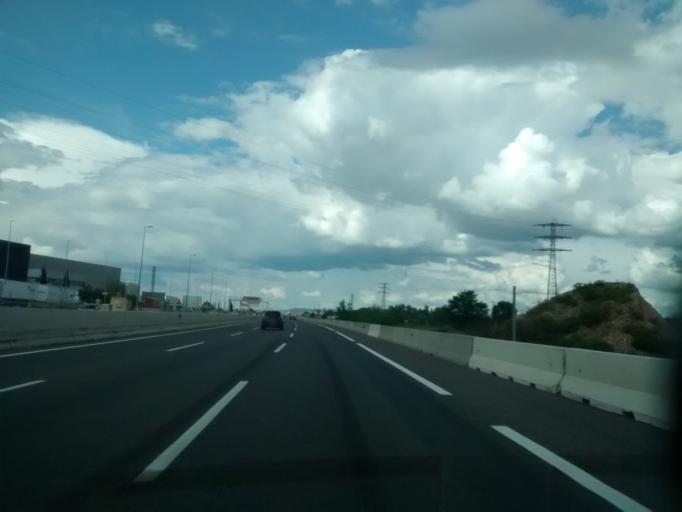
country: ES
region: Castille-La Mancha
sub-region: Provincia de Guadalajara
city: Azuqueca de Henares
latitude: 40.5731
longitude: -3.2422
